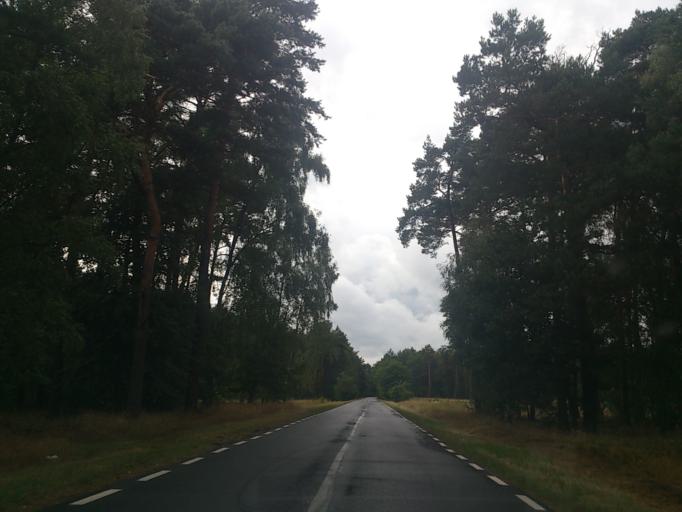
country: PL
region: Greater Poland Voivodeship
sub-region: Powiat gnieznienski
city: Kiszkowo
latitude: 52.5173
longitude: 17.1879
